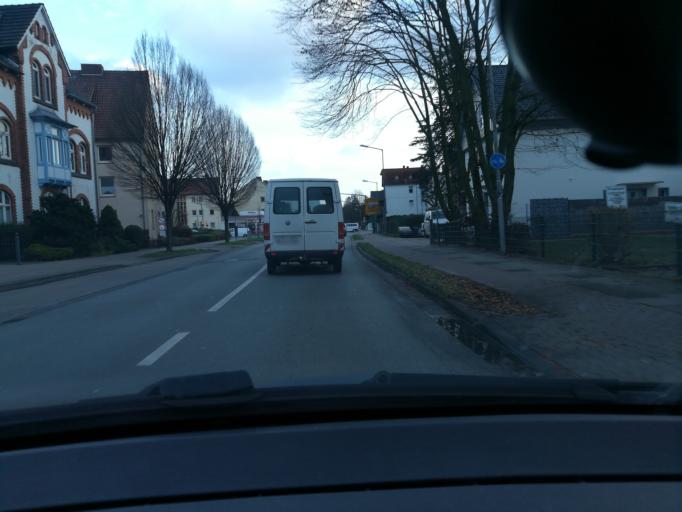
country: DE
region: North Rhine-Westphalia
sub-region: Regierungsbezirk Detmold
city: Minden
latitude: 52.2949
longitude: 8.9012
